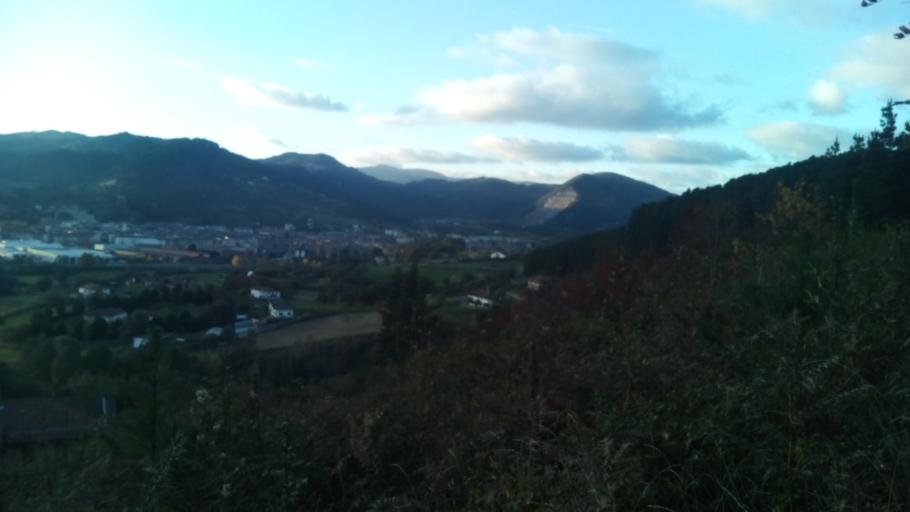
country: ES
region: Basque Country
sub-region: Bizkaia
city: Gernika-Lumo
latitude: 43.3106
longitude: -2.6600
